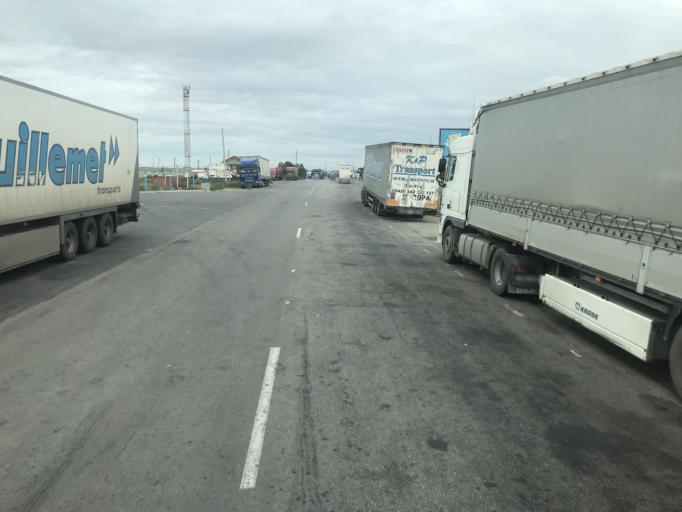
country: RU
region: Chelyabinsk
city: Bobrovka
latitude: 53.9973
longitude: 61.6443
